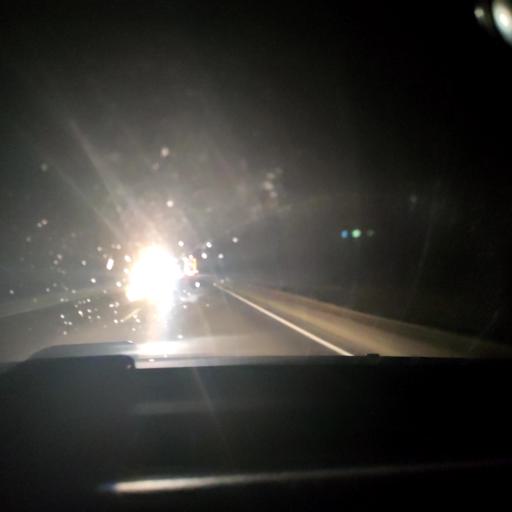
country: RU
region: Voronezj
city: Latnaya
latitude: 51.6318
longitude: 38.6645
